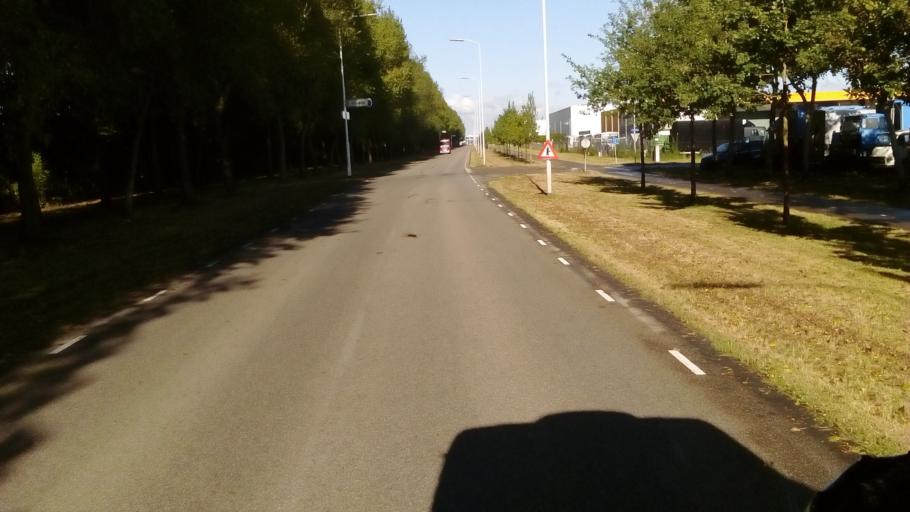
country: NL
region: North Brabant
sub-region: Gemeente Moerdijk
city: Klundert
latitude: 51.6691
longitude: 4.5537
